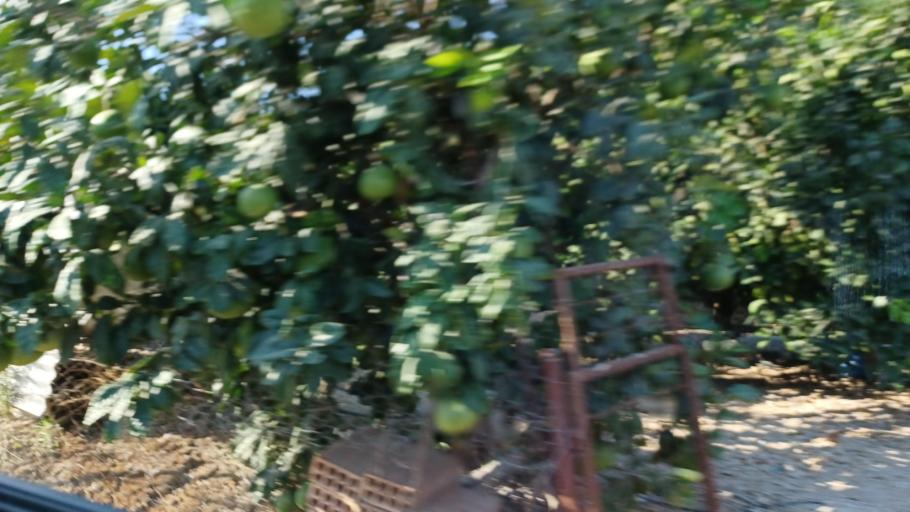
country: CY
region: Pafos
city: Tala
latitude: 34.9100
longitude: 32.4839
